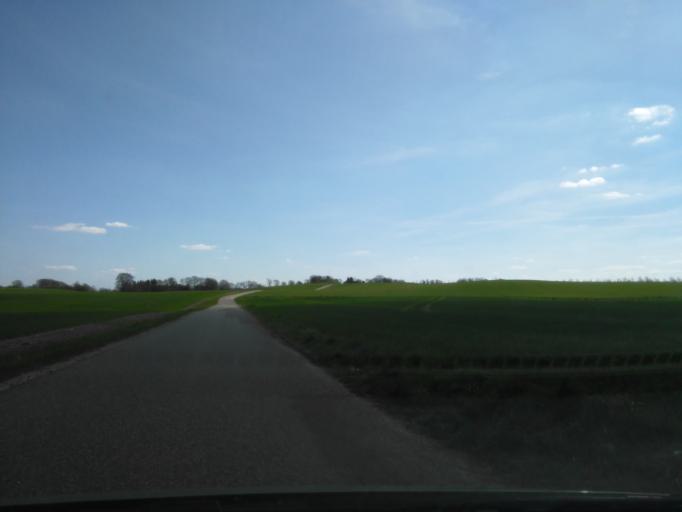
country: DK
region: Central Jutland
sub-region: Viborg Kommune
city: Viborg
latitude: 56.3578
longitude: 9.3382
